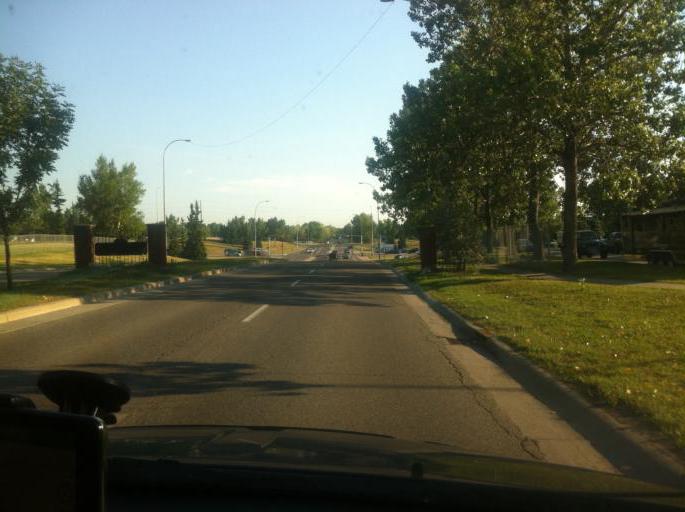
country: CA
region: Alberta
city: Calgary
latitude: 50.9456
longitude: -114.0423
